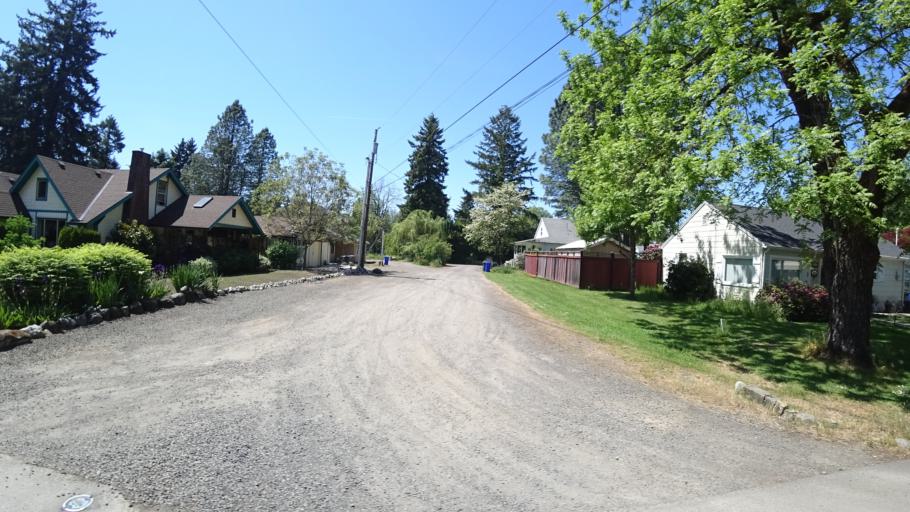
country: US
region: Oregon
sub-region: Washington County
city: Rockcreek
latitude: 45.5258
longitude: -122.9105
